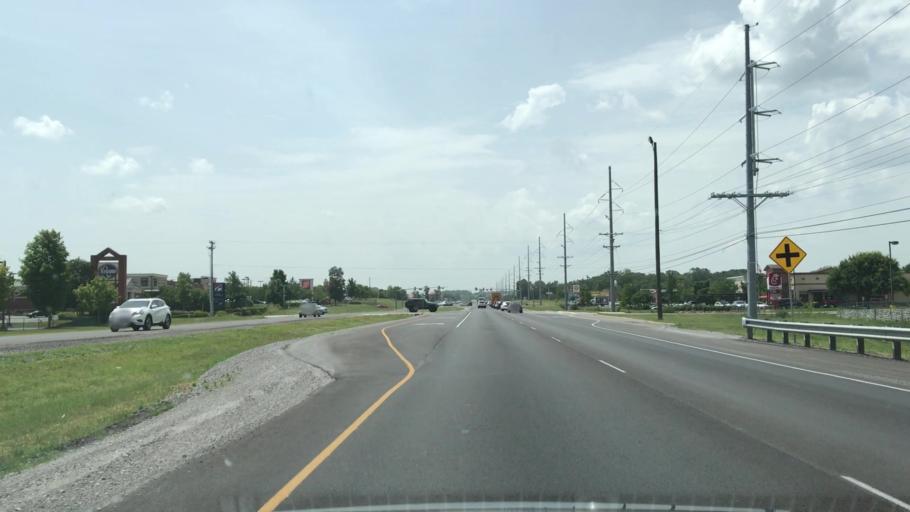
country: US
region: Tennessee
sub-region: Rutherford County
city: Smyrna
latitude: 35.9848
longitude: -86.5519
